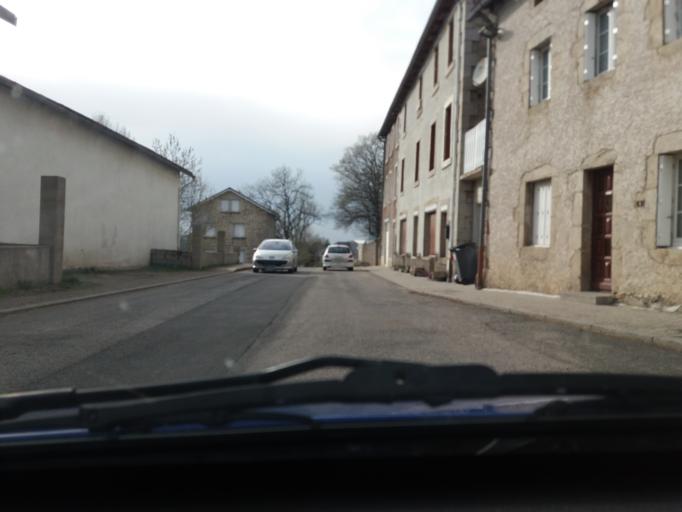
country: FR
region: Auvergne
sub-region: Departement de la Haute-Loire
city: Mazet-Saint-Voy
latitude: 45.0964
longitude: 4.2039
